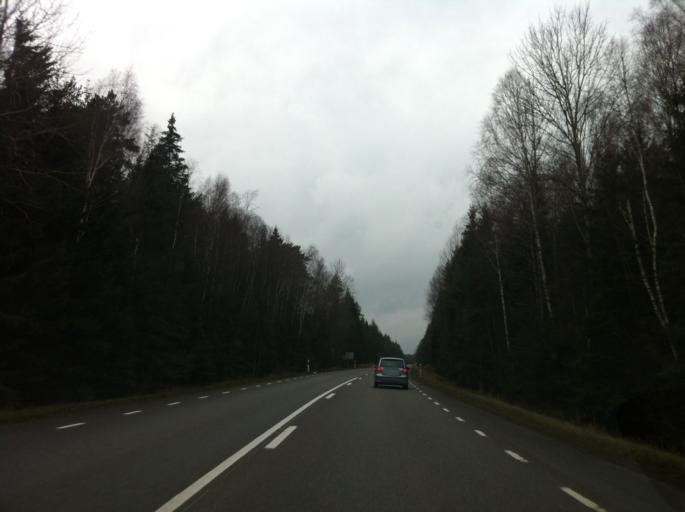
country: SE
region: Joenkoeping
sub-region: Vetlanda Kommun
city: Vetlanda
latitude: 57.4098
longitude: 14.9899
